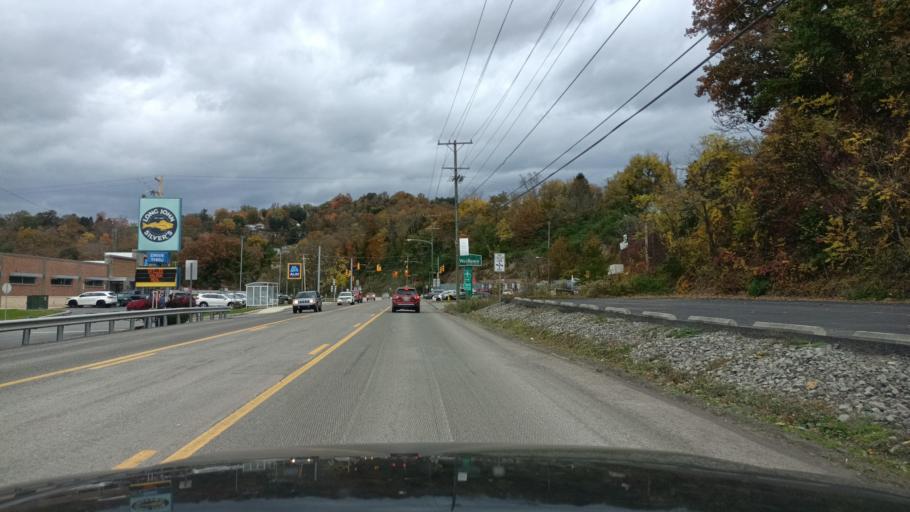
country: US
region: West Virginia
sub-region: Monongalia County
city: Morgantown
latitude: 39.6287
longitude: -79.9306
